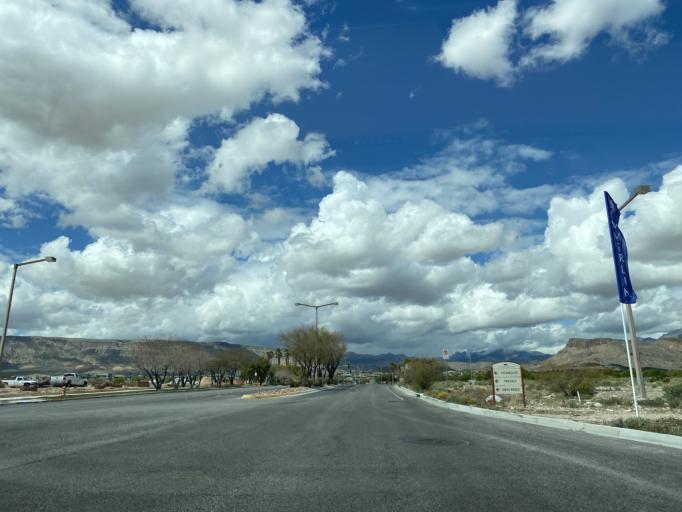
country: US
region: Nevada
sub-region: Clark County
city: Summerlin South
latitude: 36.1154
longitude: -115.3267
